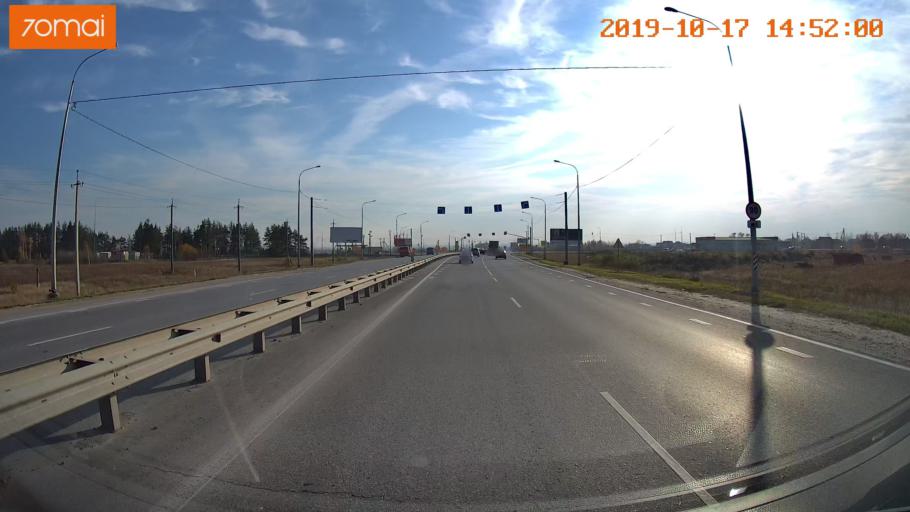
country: RU
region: Rjazan
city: Polyany
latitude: 54.7112
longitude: 39.8473
